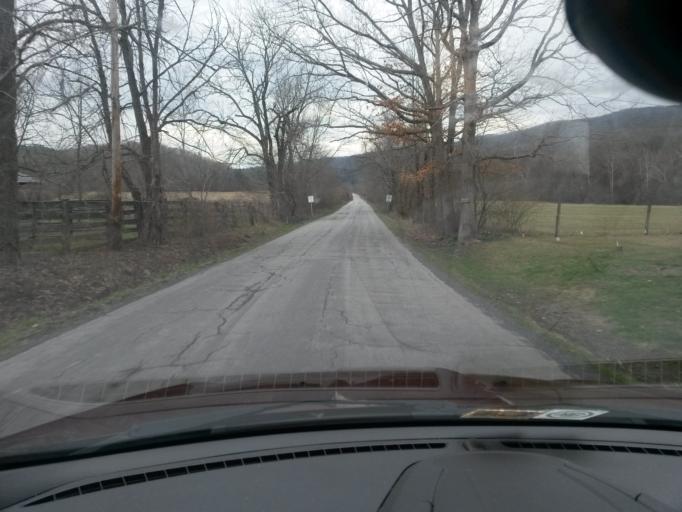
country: US
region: Virginia
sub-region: Bath County
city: Warm Springs
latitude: 38.0518
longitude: -79.8531
